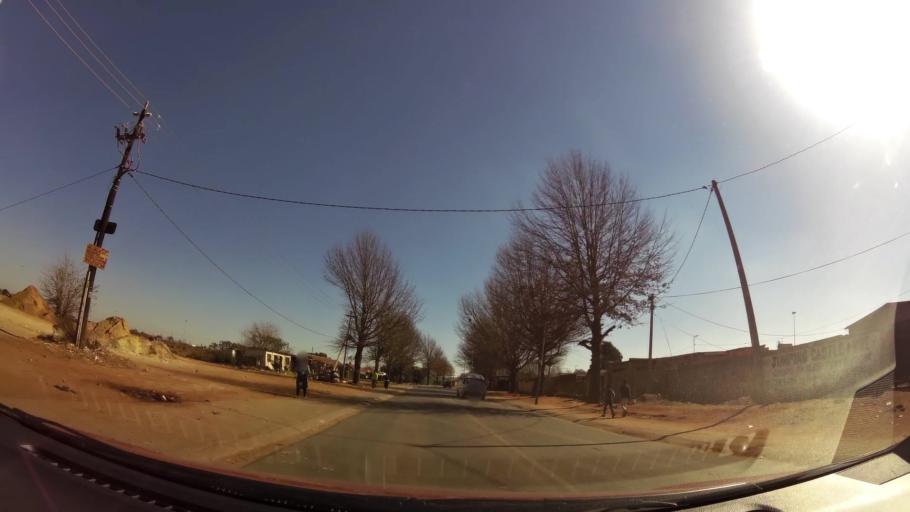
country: ZA
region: Gauteng
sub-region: City of Johannesburg Metropolitan Municipality
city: Soweto
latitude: -26.2207
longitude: 27.8338
